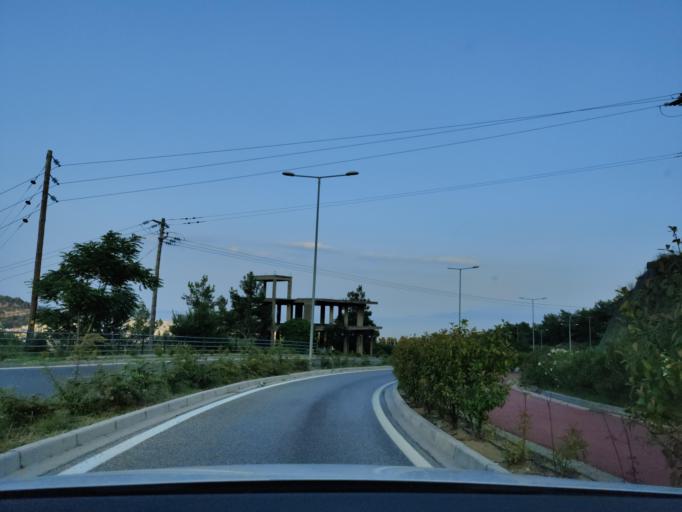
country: GR
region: East Macedonia and Thrace
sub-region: Nomos Kavalas
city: Kavala
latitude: 40.9394
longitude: 24.3796
